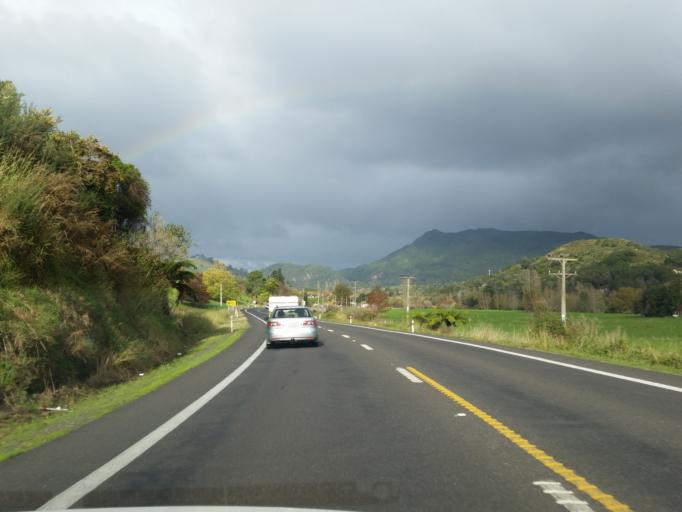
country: NZ
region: Waikato
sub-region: Hauraki District
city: Paeroa
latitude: -37.3987
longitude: 175.6943
